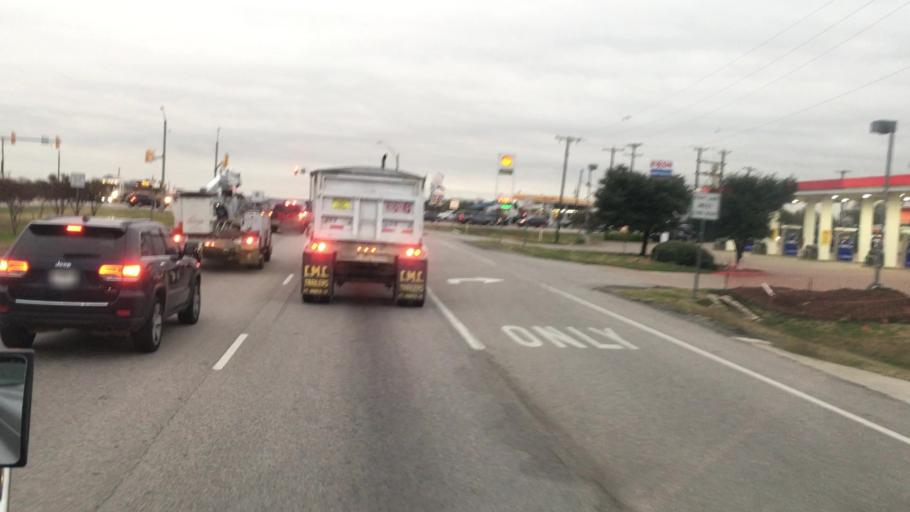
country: US
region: Texas
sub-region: Johnson County
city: Venus
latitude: 32.4357
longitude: -97.1054
